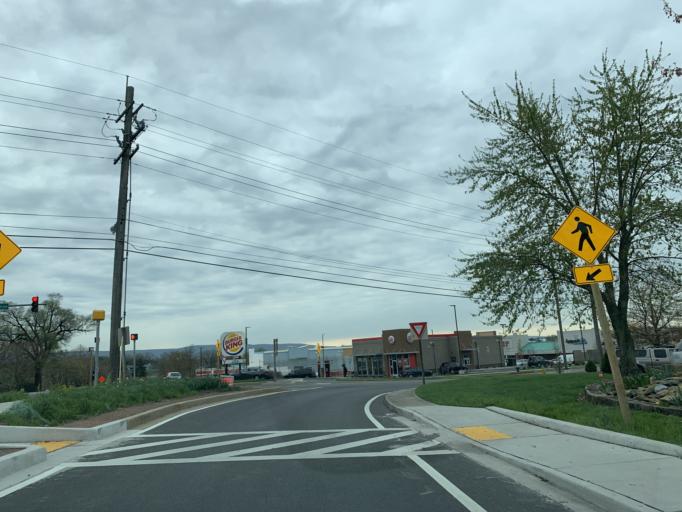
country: US
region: Maryland
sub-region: Washington County
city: Hagerstown
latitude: 39.6378
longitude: -77.7104
